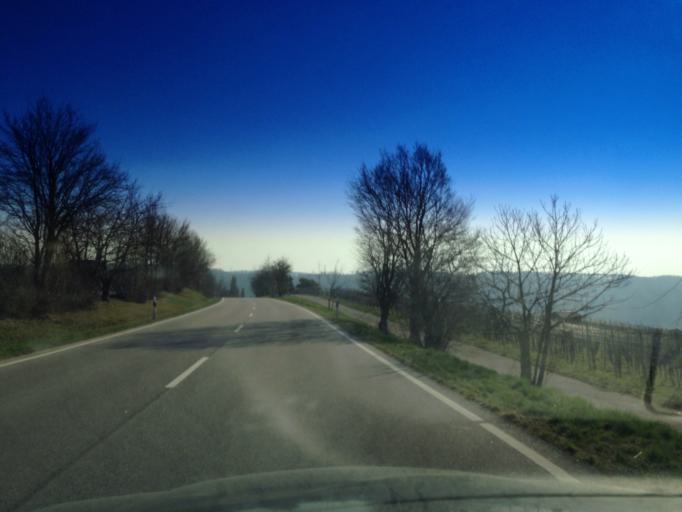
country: DE
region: Baden-Wuerttemberg
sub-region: Karlsruhe Region
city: Illingen
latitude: 48.9411
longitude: 8.9082
